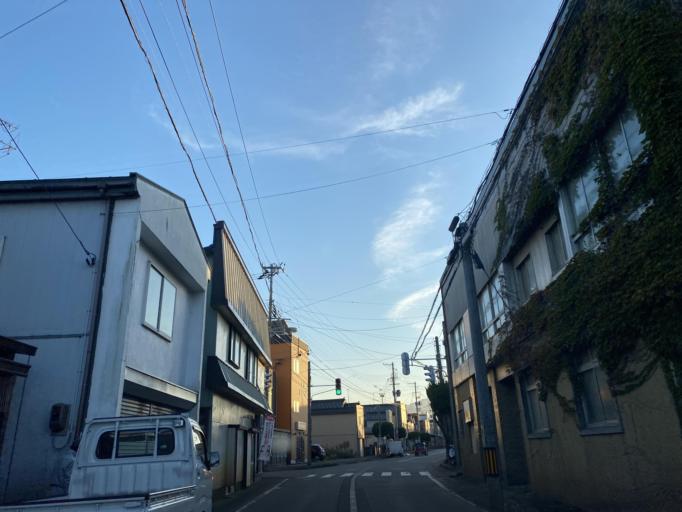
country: JP
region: Niigata
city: Kashiwazaki
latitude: 37.3757
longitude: 138.5644
